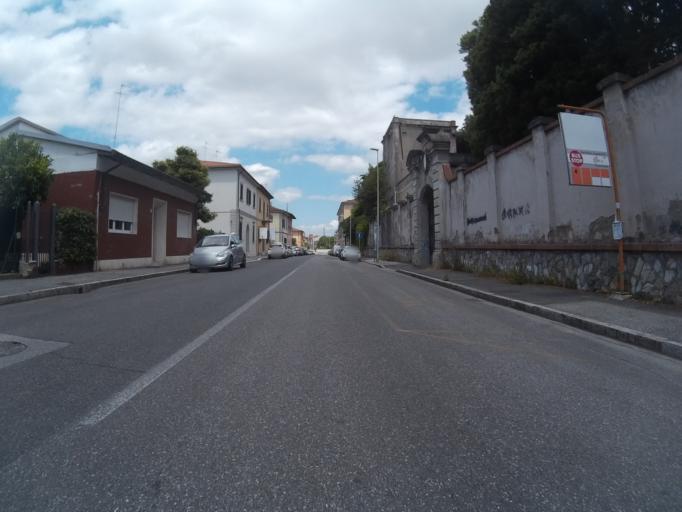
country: IT
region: Tuscany
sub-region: Provincia di Livorno
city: Livorno
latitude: 43.5659
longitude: 10.3315
